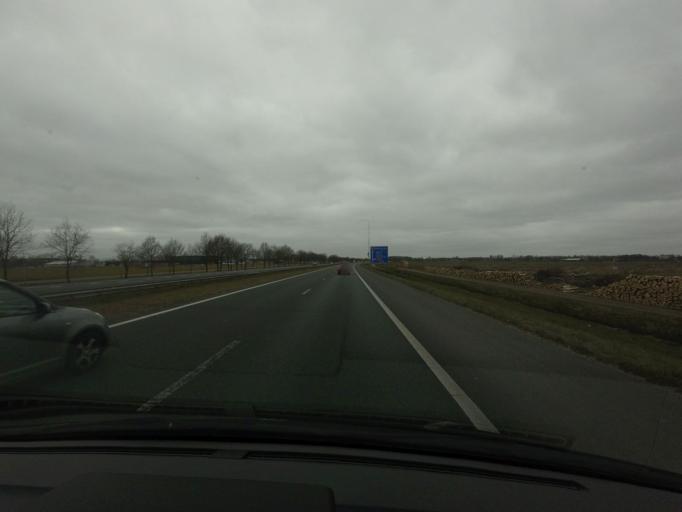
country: NL
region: Groningen
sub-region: Gemeente Hoogezand-Sappemeer
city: Hoogezand
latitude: 53.1721
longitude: 6.7478
